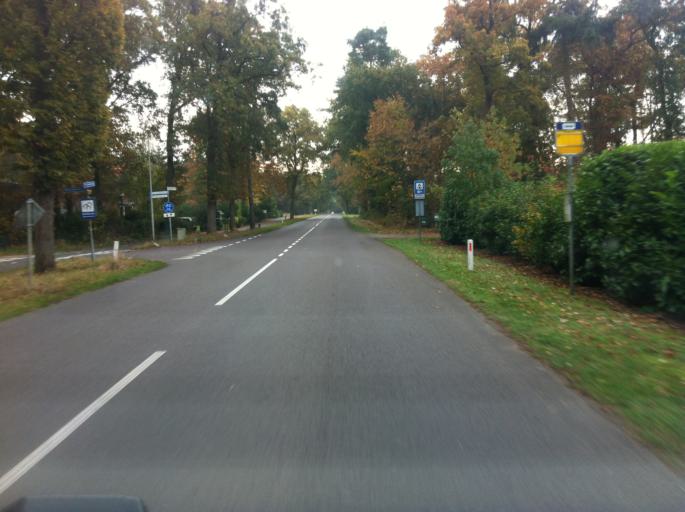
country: NL
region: Overijssel
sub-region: Gemeente Enschede
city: Enschede
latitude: 52.1391
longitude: 6.8487
